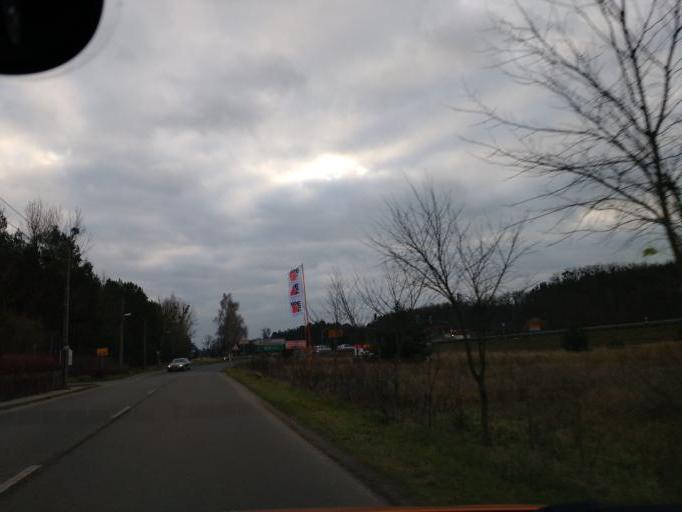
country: DE
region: Brandenburg
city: Wriezen
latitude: 52.6998
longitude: 14.1359
